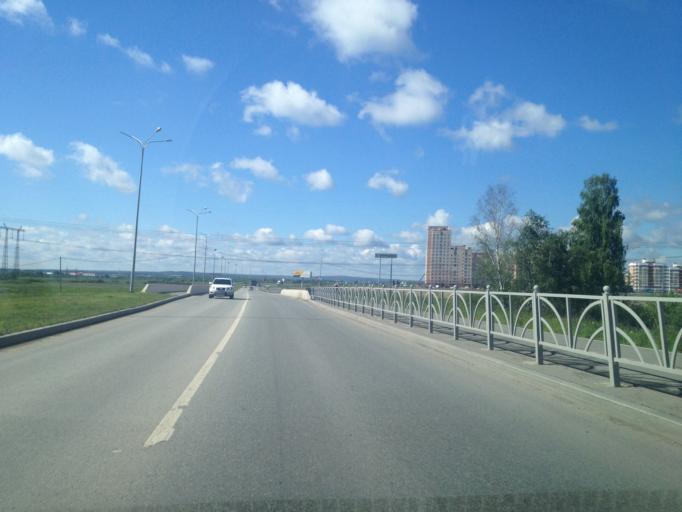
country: RU
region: Sverdlovsk
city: Sovkhoznyy
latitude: 56.7499
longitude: 60.5770
